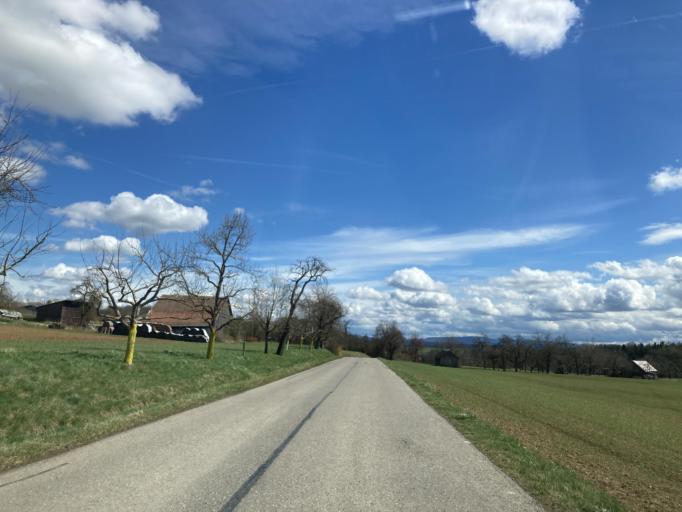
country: DE
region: Baden-Wuerttemberg
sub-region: Tuebingen Region
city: Hirrlingen
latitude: 48.4558
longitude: 8.8454
